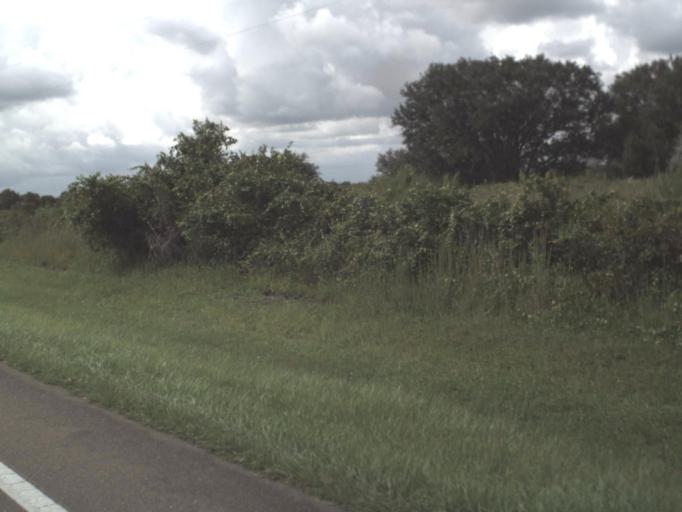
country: US
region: Florida
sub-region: Sarasota County
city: North Port
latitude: 27.1934
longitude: -82.0899
